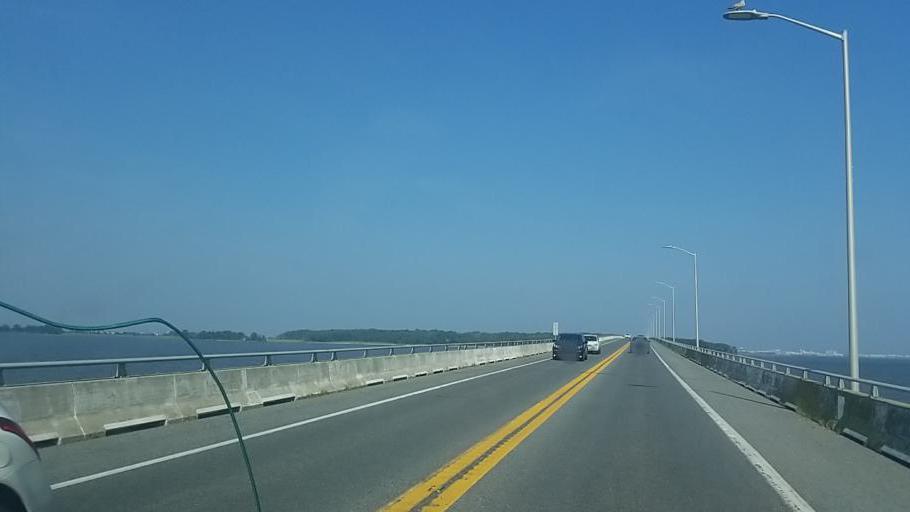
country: US
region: Maryland
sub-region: Worcester County
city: Ocean Pines
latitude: 38.3895
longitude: -75.1263
